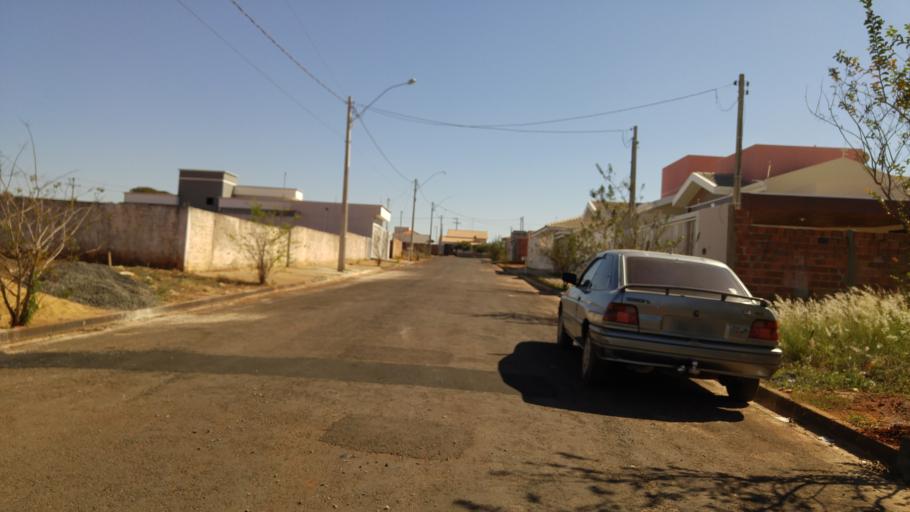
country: BR
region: Sao Paulo
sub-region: Paraguacu Paulista
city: Paraguacu Paulista
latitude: -22.4405
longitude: -50.5878
